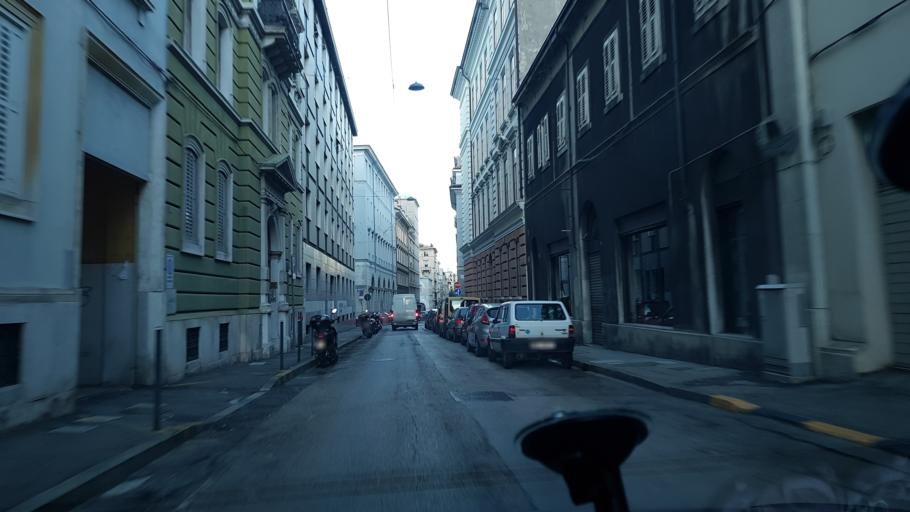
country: IT
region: Friuli Venezia Giulia
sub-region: Provincia di Trieste
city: Trieste
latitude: 45.6547
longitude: 13.7821
